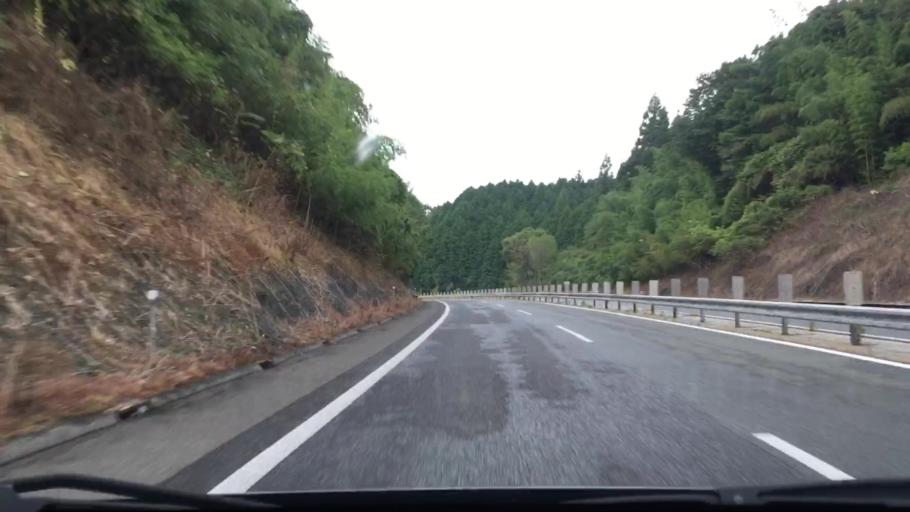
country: JP
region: Okayama
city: Niimi
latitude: 34.9110
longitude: 133.3048
